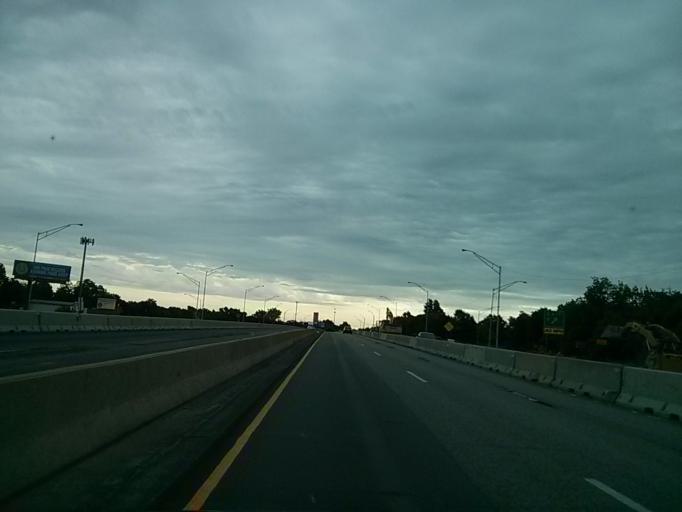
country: US
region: Oklahoma
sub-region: Tulsa County
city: Tulsa
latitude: 36.1603
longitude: -95.9532
